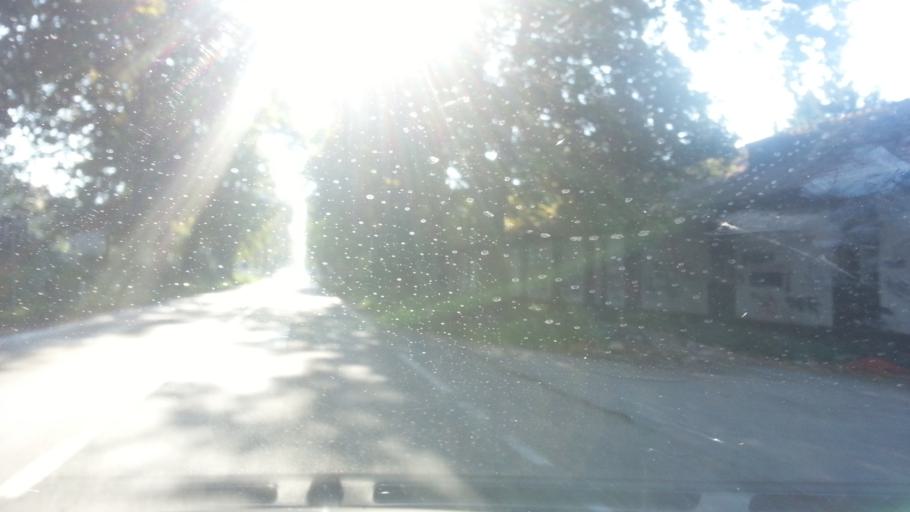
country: RS
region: Central Serbia
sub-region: Belgrade
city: Zemun
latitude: 44.8647
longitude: 20.3651
